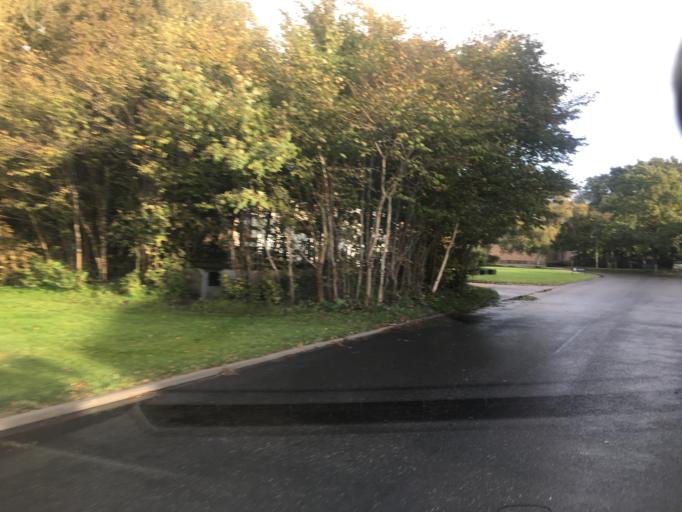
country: DK
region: South Denmark
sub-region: Tonder Kommune
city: Tonder
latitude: 54.9508
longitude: 8.8772
